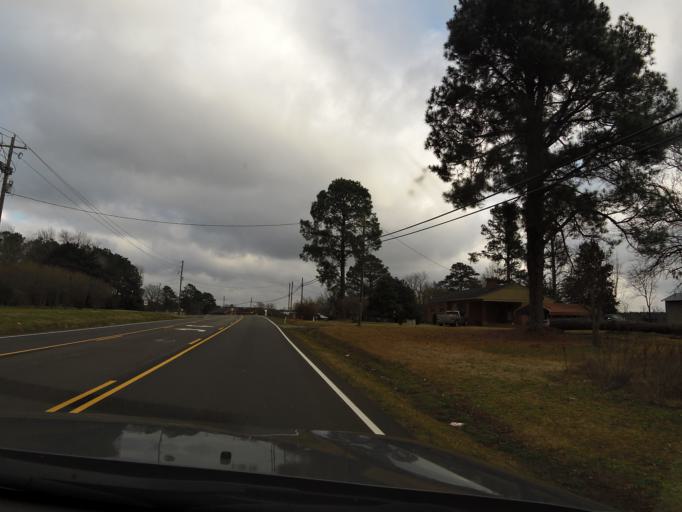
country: US
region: North Carolina
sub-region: Nash County
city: Rocky Mount
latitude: 35.9169
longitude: -77.7624
